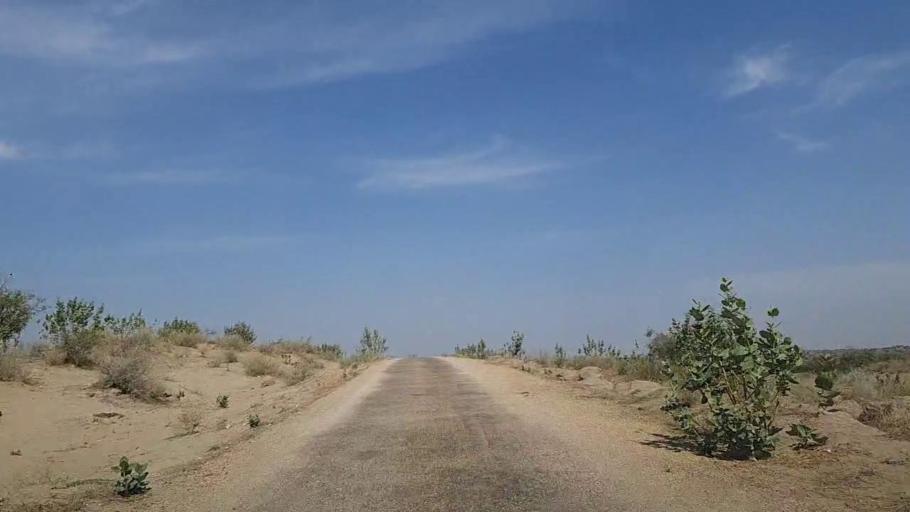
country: PK
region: Sindh
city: Umarkot
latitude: 25.2480
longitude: 69.9018
